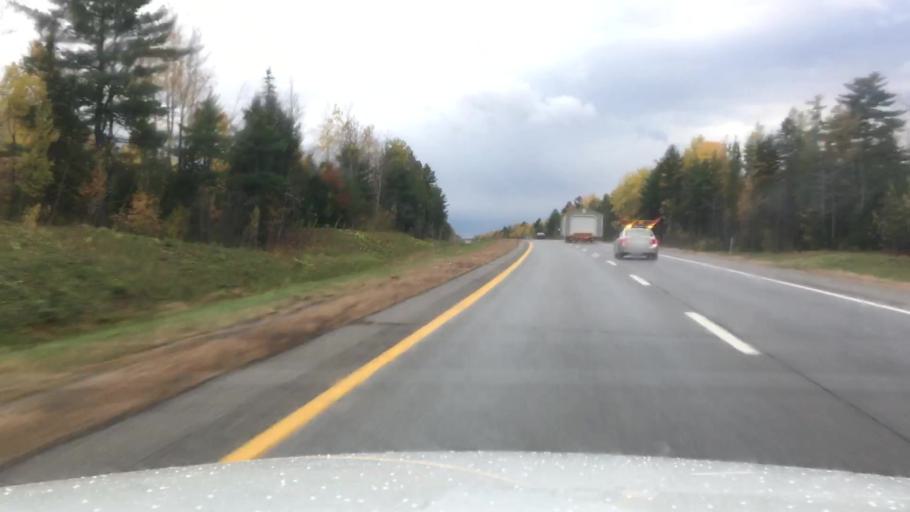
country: US
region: Maine
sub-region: Penobscot County
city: Howland
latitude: 45.2616
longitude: -68.6809
